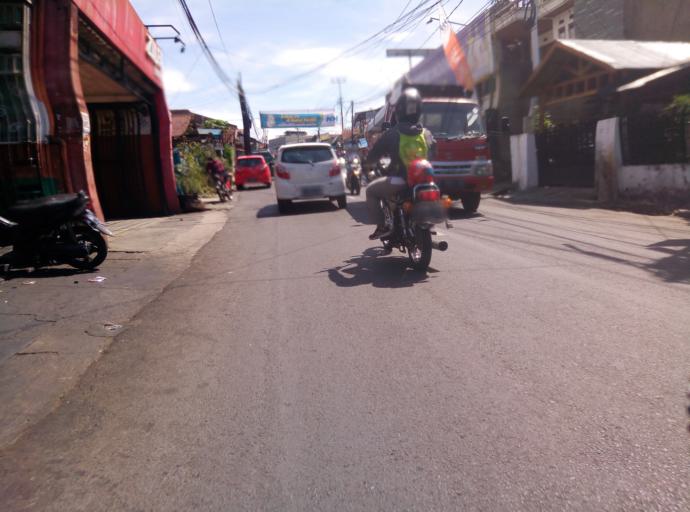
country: ID
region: West Java
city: Bandung
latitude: -6.8922
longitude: 107.6305
